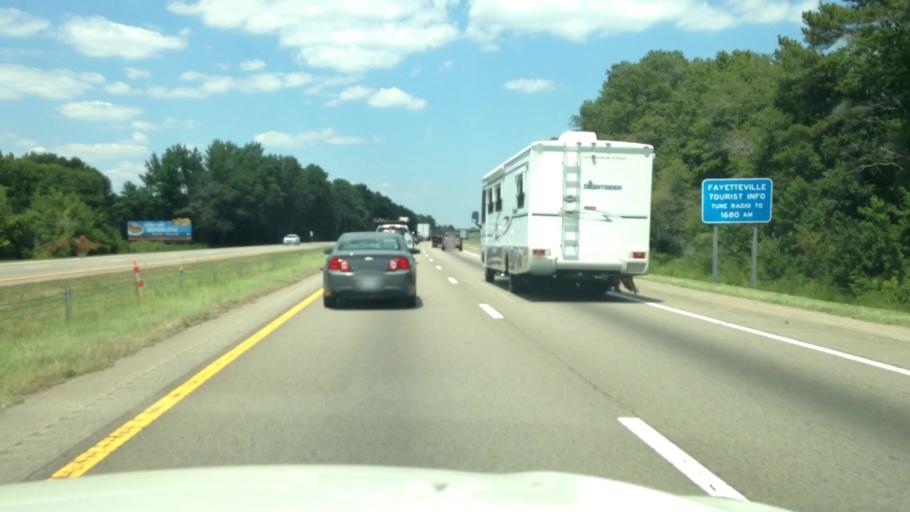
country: US
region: North Carolina
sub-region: Cumberland County
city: Hope Mills
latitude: 34.9148
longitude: -78.9521
